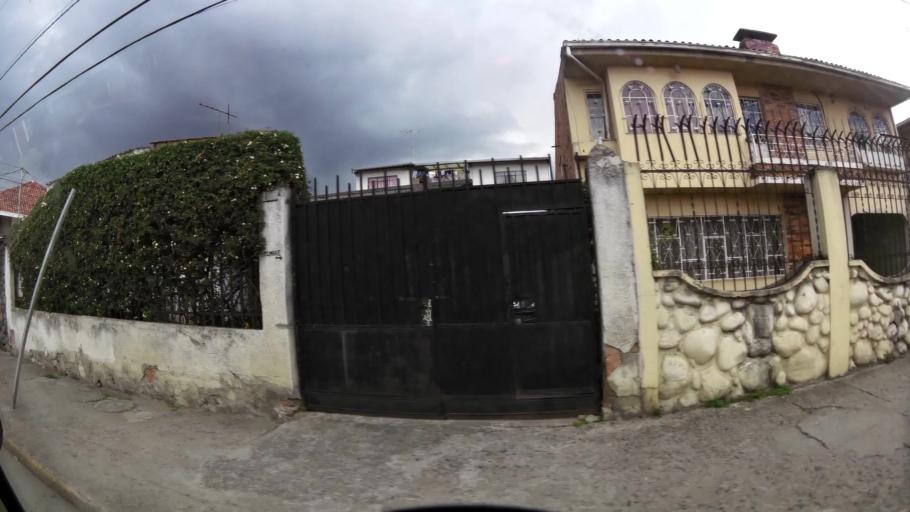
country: EC
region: Azuay
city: Cuenca
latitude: -2.8896
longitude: -79.0191
